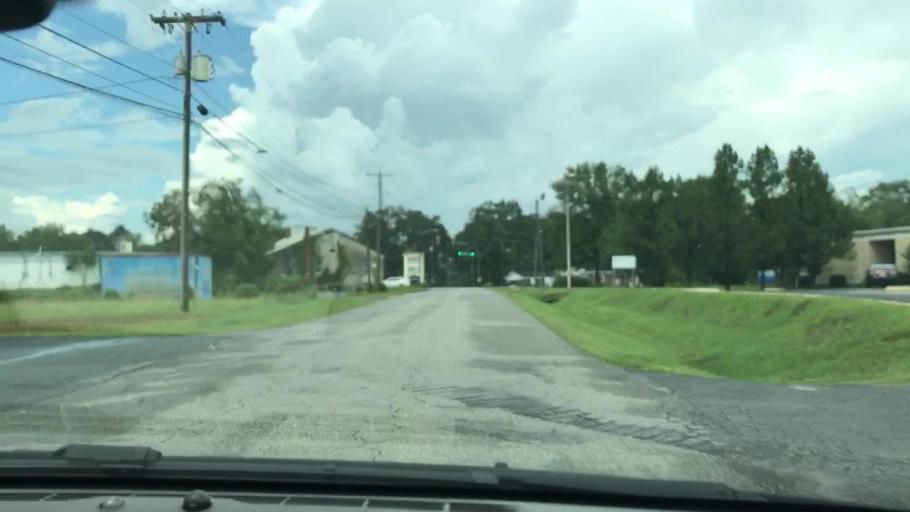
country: US
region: Georgia
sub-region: Early County
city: Blakely
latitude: 31.3717
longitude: -84.9469
